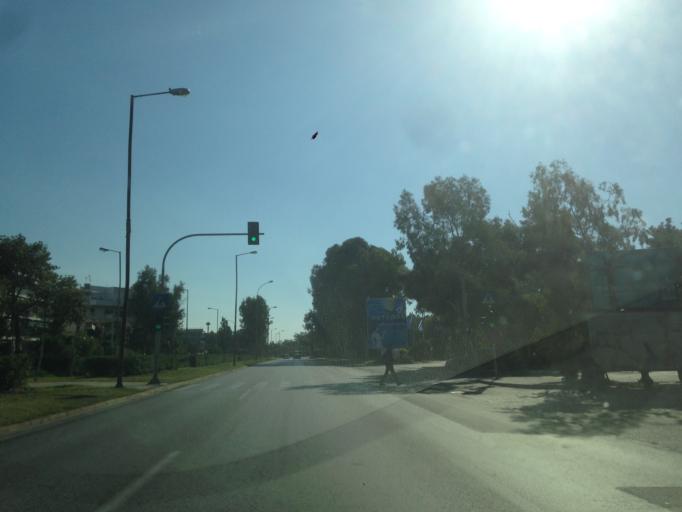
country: GR
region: Attica
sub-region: Nomarchia Athinas
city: Glyfada
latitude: 37.8565
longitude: 23.7518
